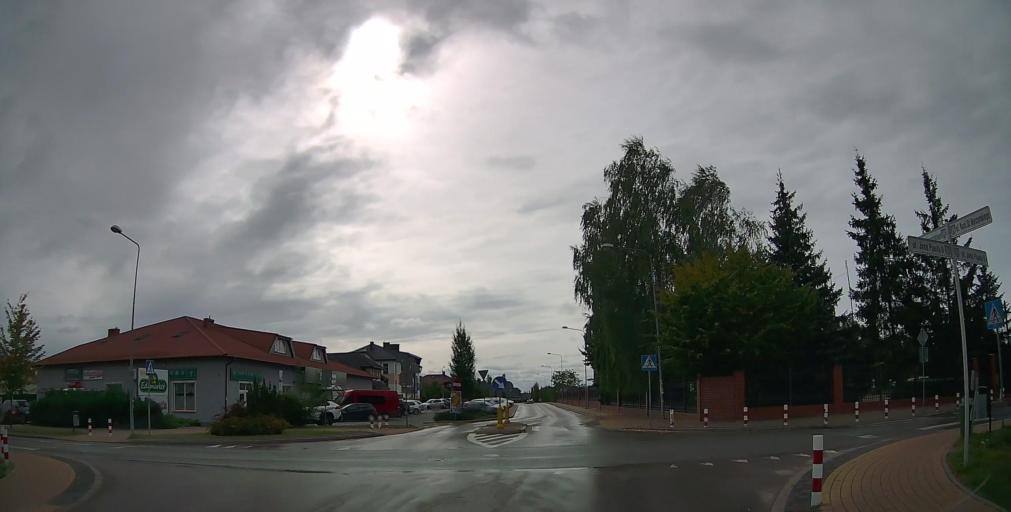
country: PL
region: Masovian Voivodeship
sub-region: Powiat grojecki
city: Grojec
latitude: 51.8625
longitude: 20.8756
